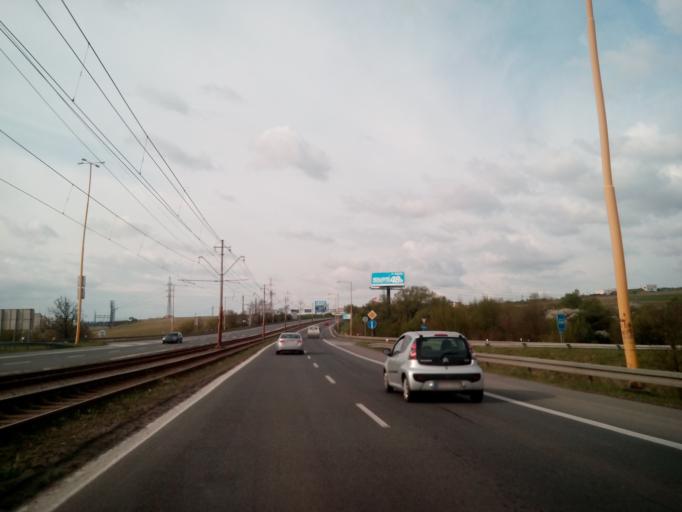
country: SK
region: Kosicky
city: Kosice
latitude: 48.6933
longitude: 21.2320
